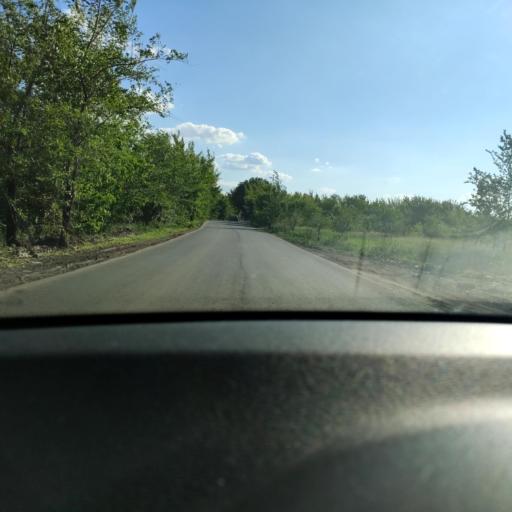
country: RU
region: Samara
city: Smyshlyayevka
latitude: 53.2457
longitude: 50.3639
